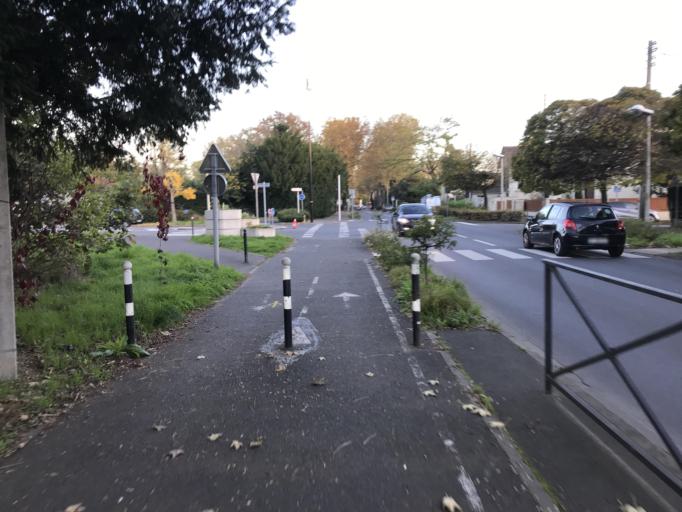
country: FR
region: Ile-de-France
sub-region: Departement de l'Essonne
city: Athis-Mons
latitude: 48.7113
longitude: 2.3824
